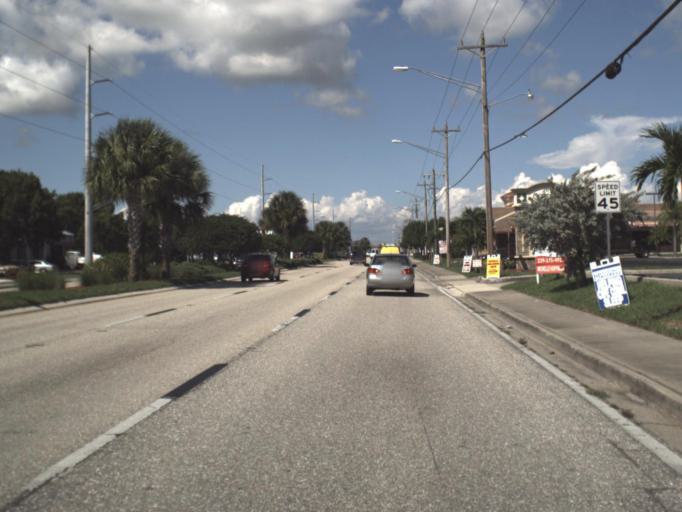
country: US
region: Florida
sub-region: Lee County
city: Lochmoor Waterway Estates
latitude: 26.6460
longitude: -81.9409
